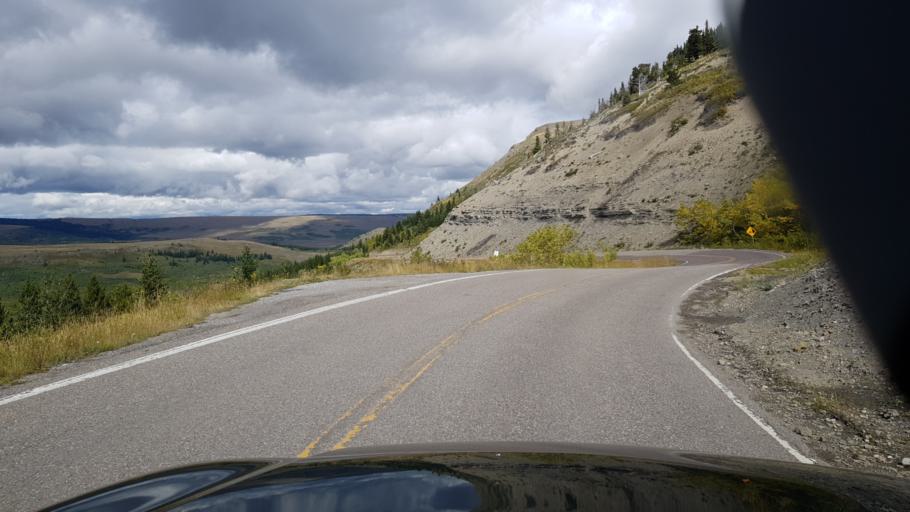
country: US
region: Montana
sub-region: Glacier County
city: South Browning
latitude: 48.5326
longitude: -113.3074
